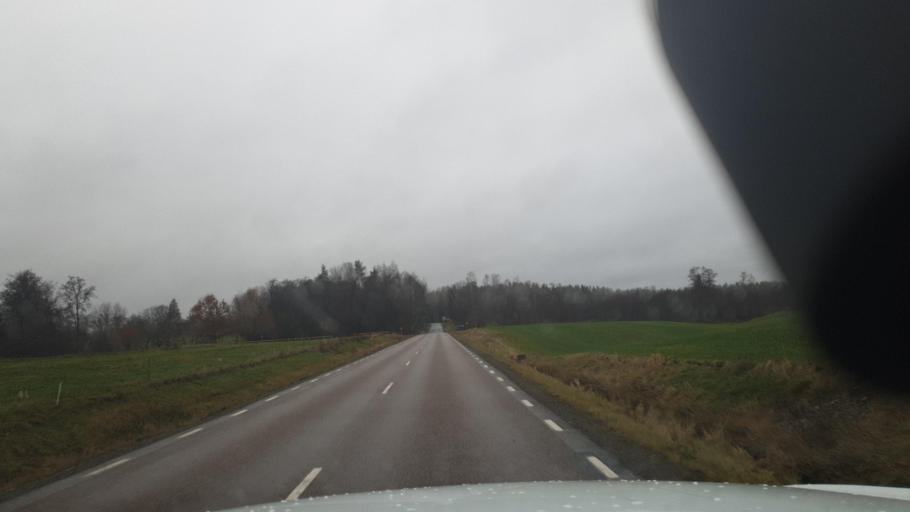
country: SE
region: Vaermland
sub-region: Arvika Kommun
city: Arvika
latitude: 59.5261
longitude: 12.6193
